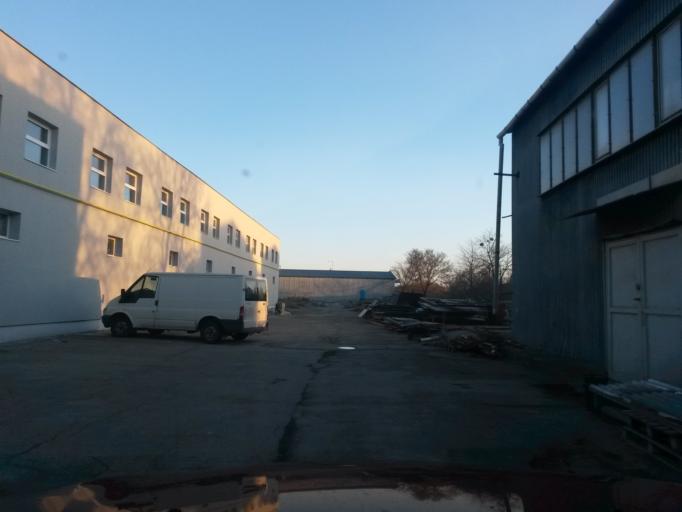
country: SK
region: Kosicky
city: Kosice
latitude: 48.7268
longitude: 21.2735
